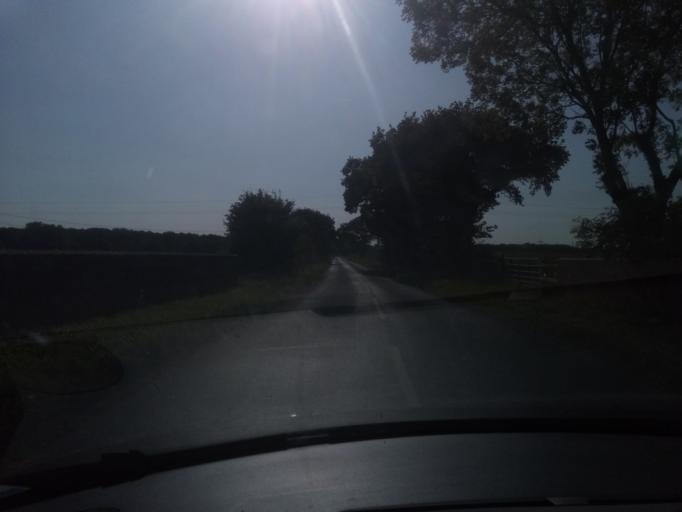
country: GB
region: England
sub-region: North Yorkshire
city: Camblesforth
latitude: 53.7456
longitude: -1.0338
